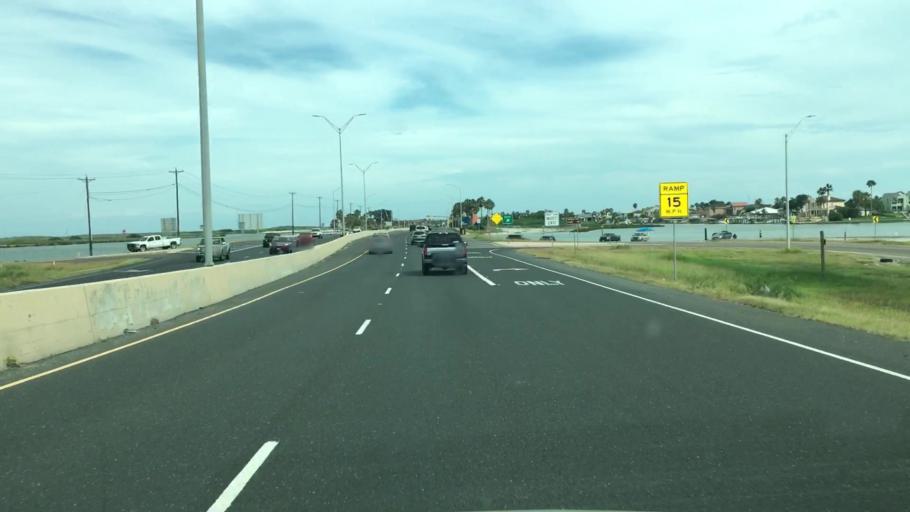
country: US
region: Texas
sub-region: Nueces County
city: Corpus Christi
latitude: 27.6325
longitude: -97.2347
